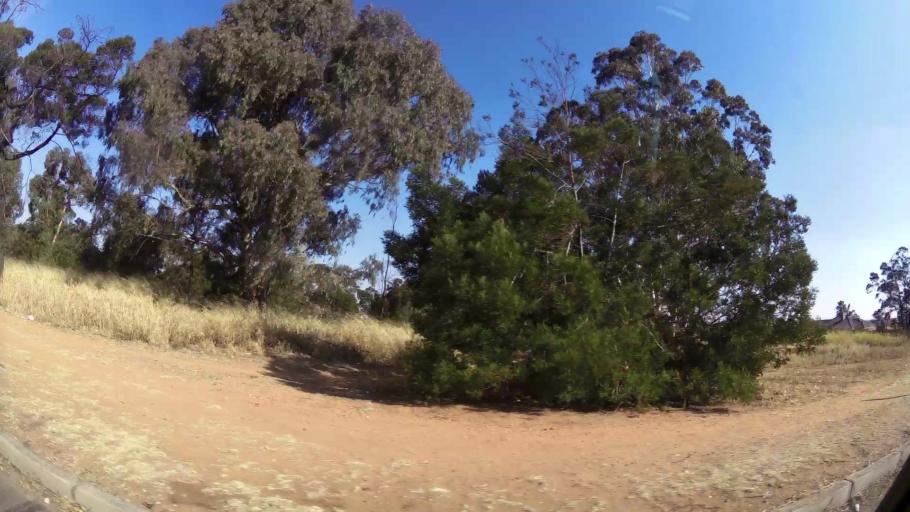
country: ZA
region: Gauteng
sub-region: City of Johannesburg Metropolitan Municipality
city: Johannesburg
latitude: -26.2597
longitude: 28.0186
